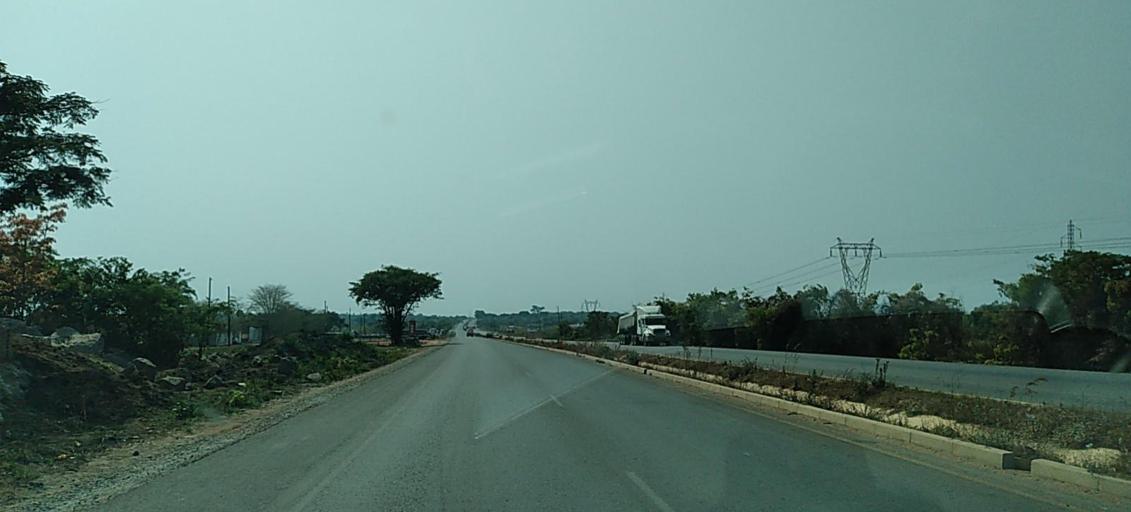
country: ZM
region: Copperbelt
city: Chingola
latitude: -12.5729
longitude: 27.9130
